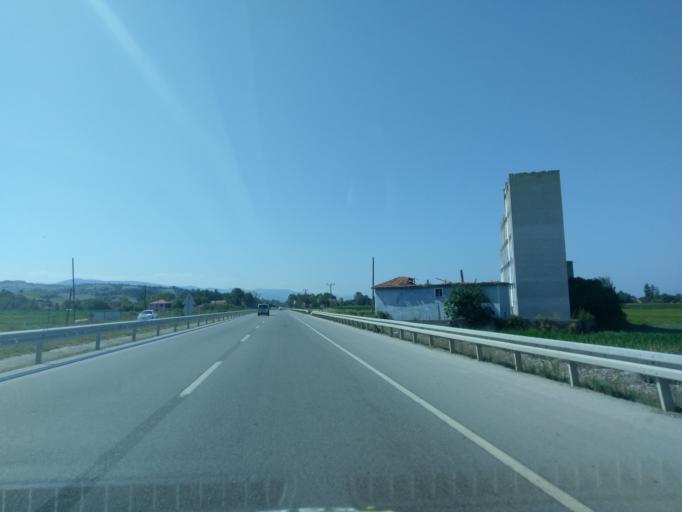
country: TR
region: Samsun
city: Alacam
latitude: 41.6095
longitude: 35.6573
